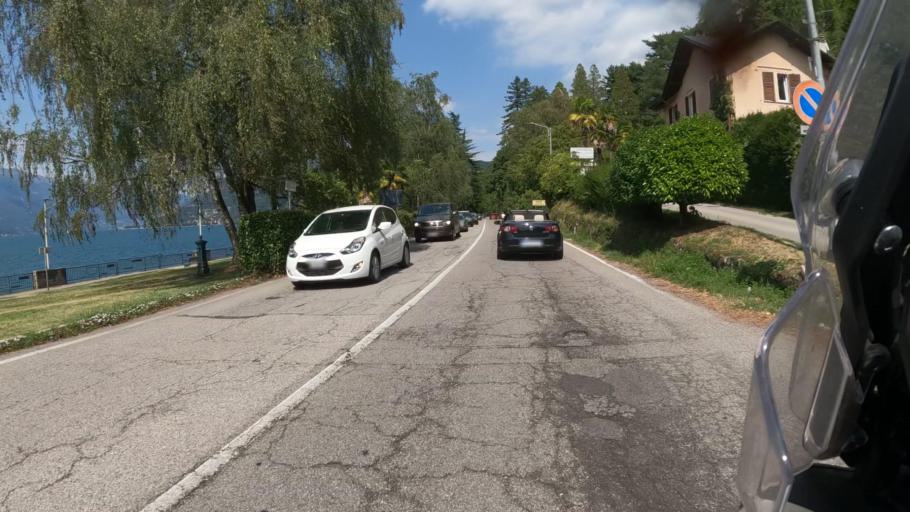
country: IT
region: Lombardy
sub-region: Provincia di Varese
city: Luino
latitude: 46.0049
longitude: 8.7442
